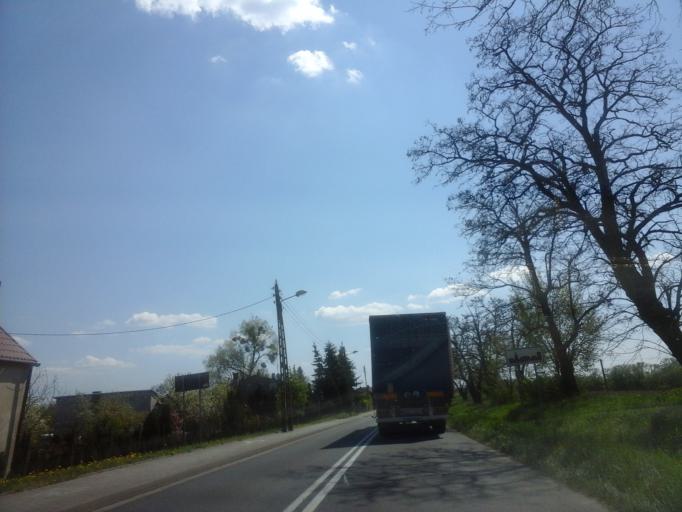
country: PL
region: West Pomeranian Voivodeship
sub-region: Powiat choszczenski
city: Bierzwnik
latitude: 53.0481
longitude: 15.6661
